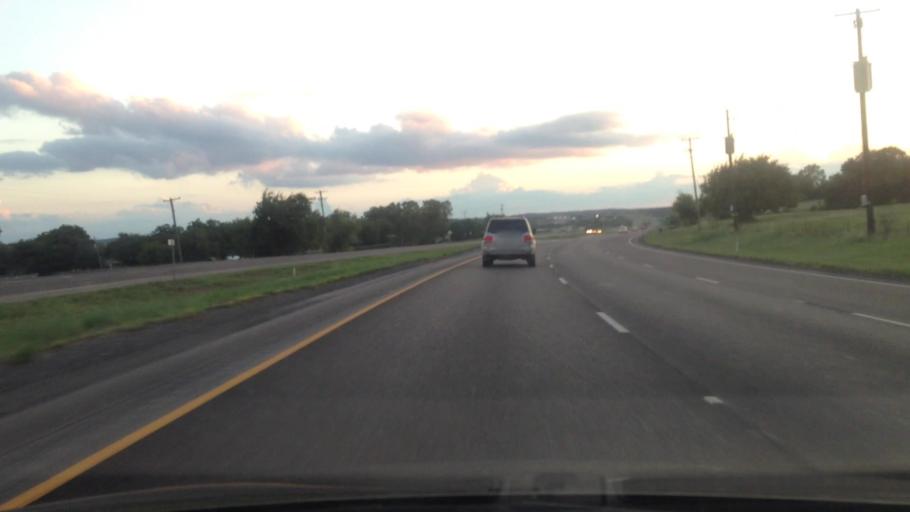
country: US
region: Texas
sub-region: Parker County
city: Aledo
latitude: 32.6042
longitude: -97.5595
